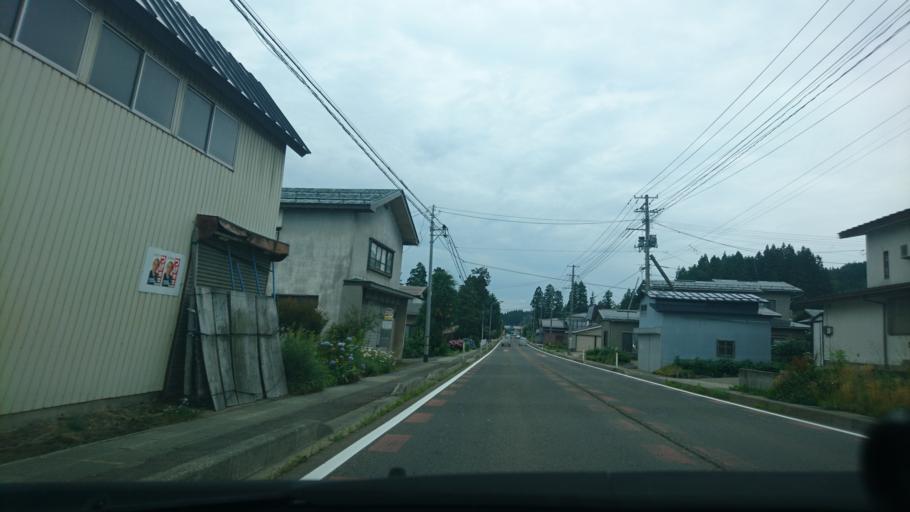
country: JP
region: Akita
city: Yokotemachi
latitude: 39.3659
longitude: 140.5667
